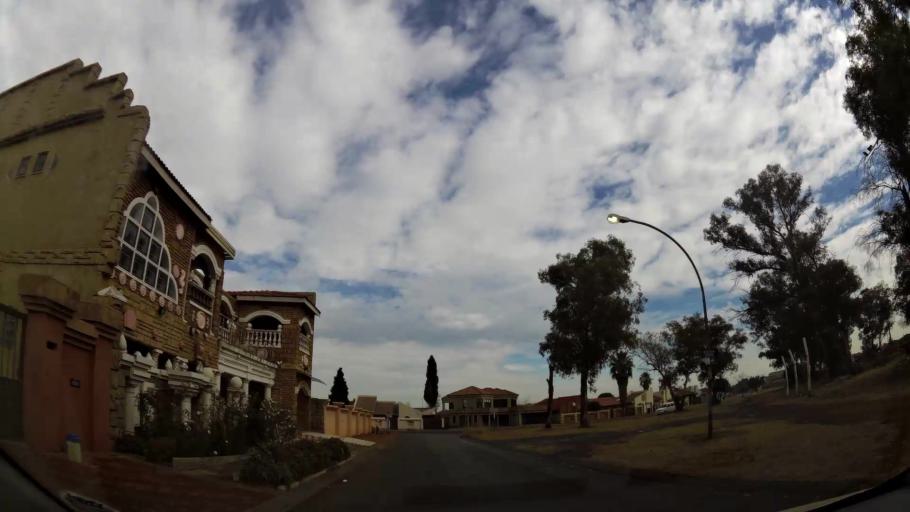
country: ZA
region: Gauteng
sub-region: Ekurhuleni Metropolitan Municipality
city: Germiston
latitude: -26.3220
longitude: 28.1836
